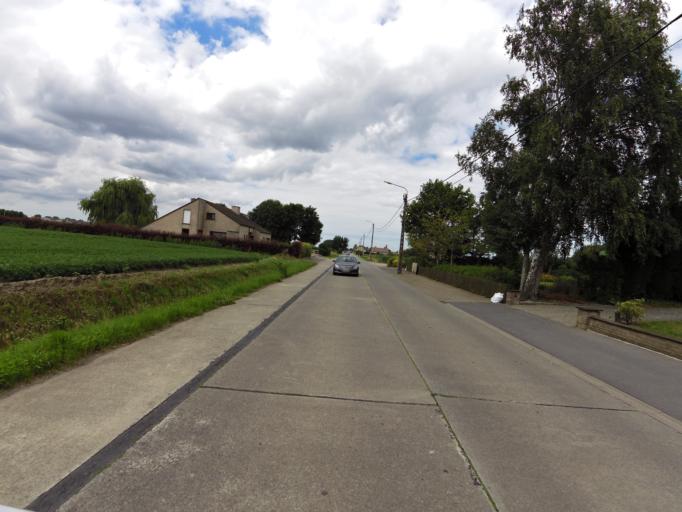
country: BE
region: Flanders
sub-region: Provincie West-Vlaanderen
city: Ichtegem
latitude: 51.0602
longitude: 3.0061
